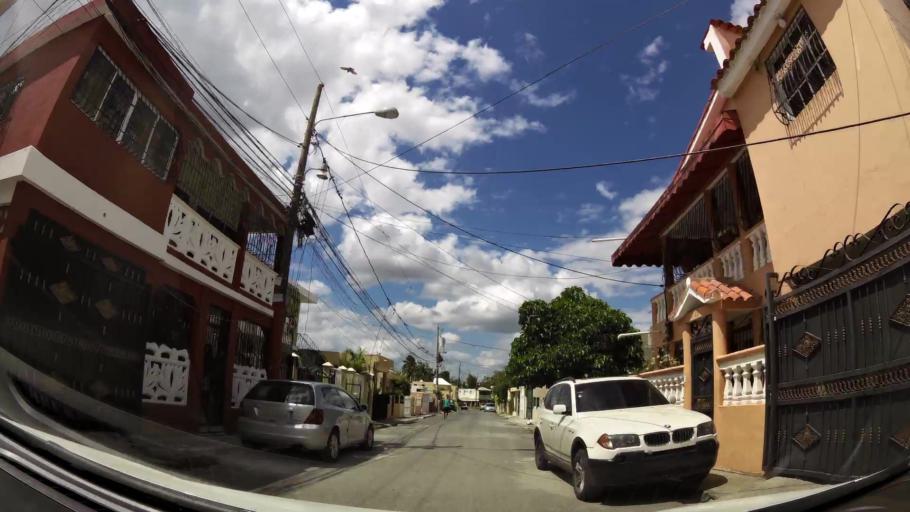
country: DO
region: Nacional
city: Ensanche Luperon
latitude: 18.5258
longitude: -69.8986
